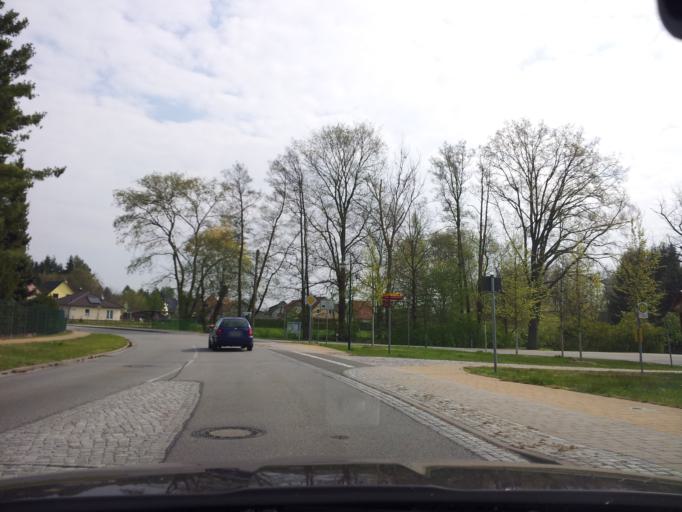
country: DE
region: Brandenburg
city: Rehfelde
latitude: 52.4570
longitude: 13.9083
